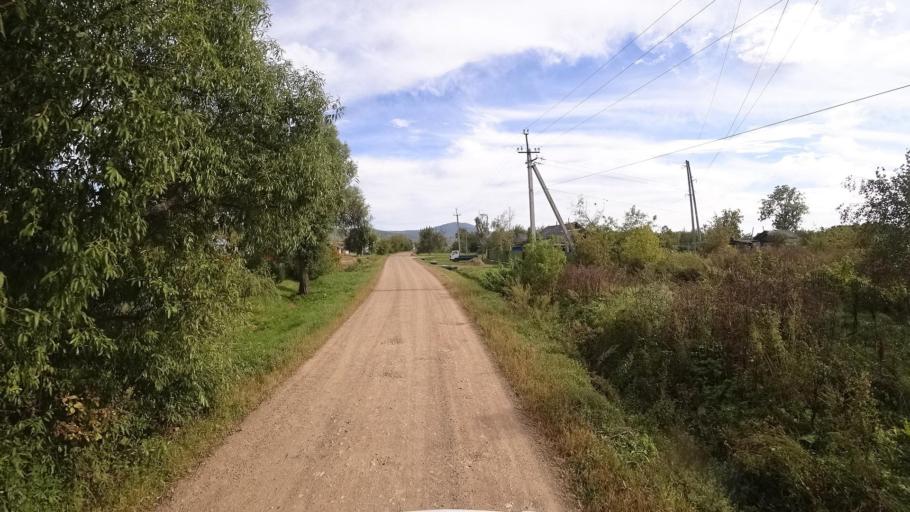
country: RU
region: Primorskiy
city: Dostoyevka
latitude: 44.3042
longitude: 133.4611
